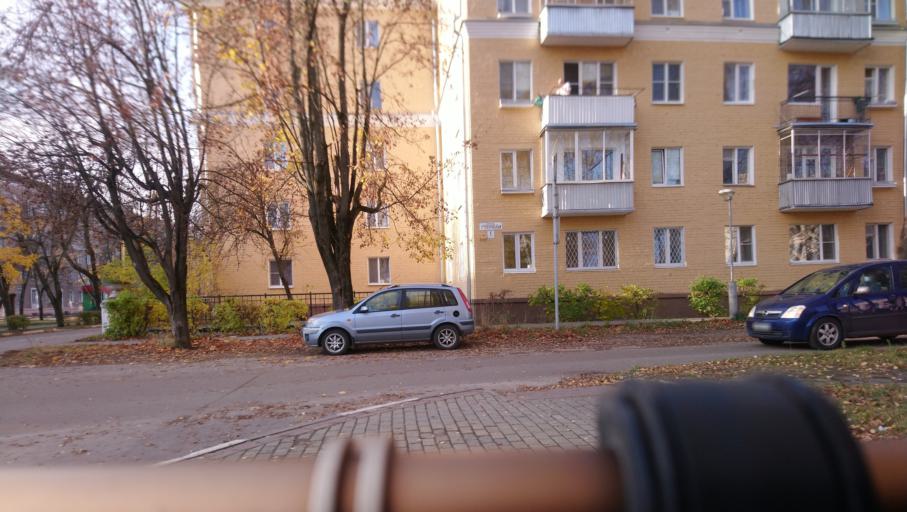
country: RU
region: Moskovskaya
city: Dubna
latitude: 56.7565
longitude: 37.1313
